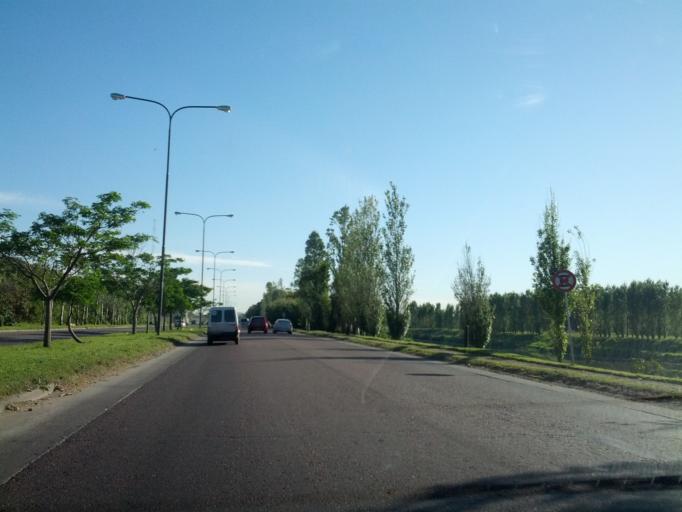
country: AR
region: Buenos Aires F.D.
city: Villa Lugano
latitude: -34.6782
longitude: -58.4387
